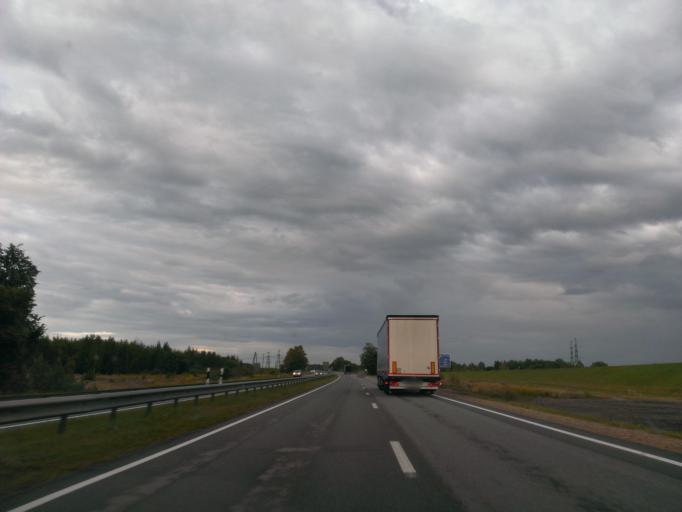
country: LV
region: Salaspils
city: Salaspils
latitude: 56.8466
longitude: 24.3625
